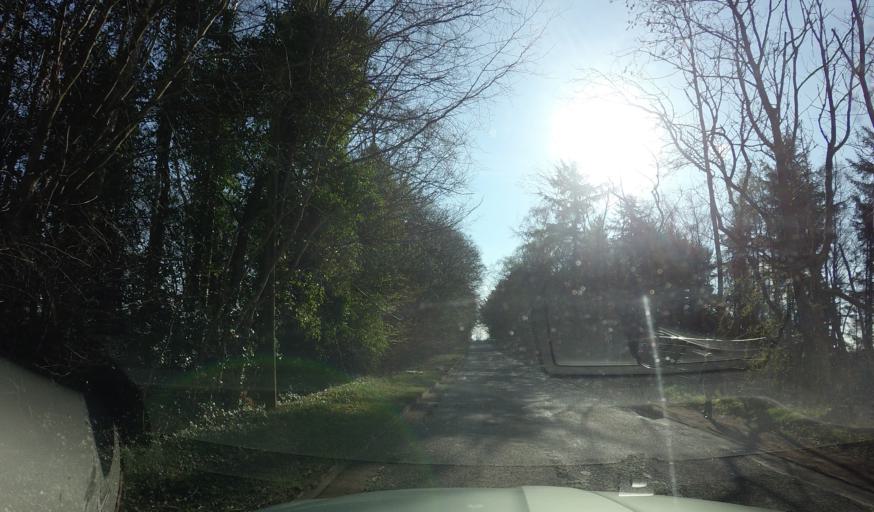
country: GB
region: Scotland
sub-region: Midlothian
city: Penicuik
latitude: 55.8477
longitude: -3.2214
